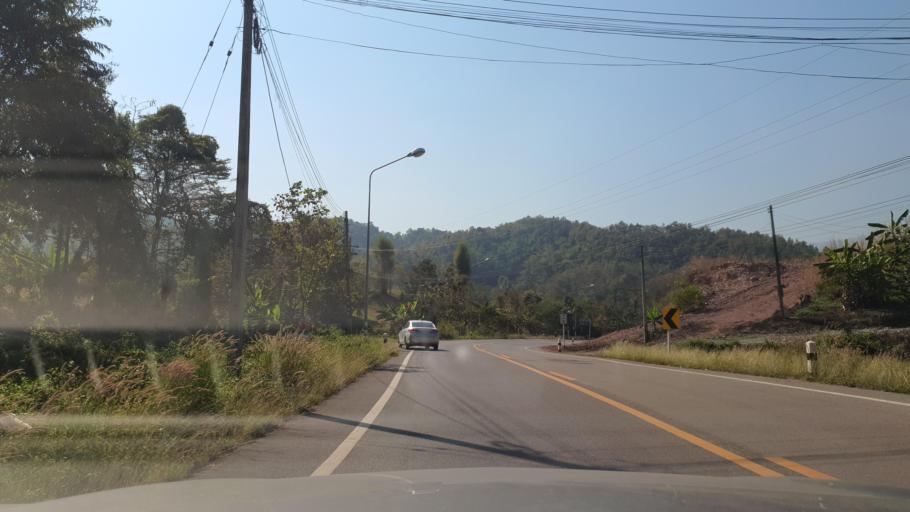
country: TH
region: Chiang Rai
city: Mae Lao
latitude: 19.8336
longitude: 99.6849
